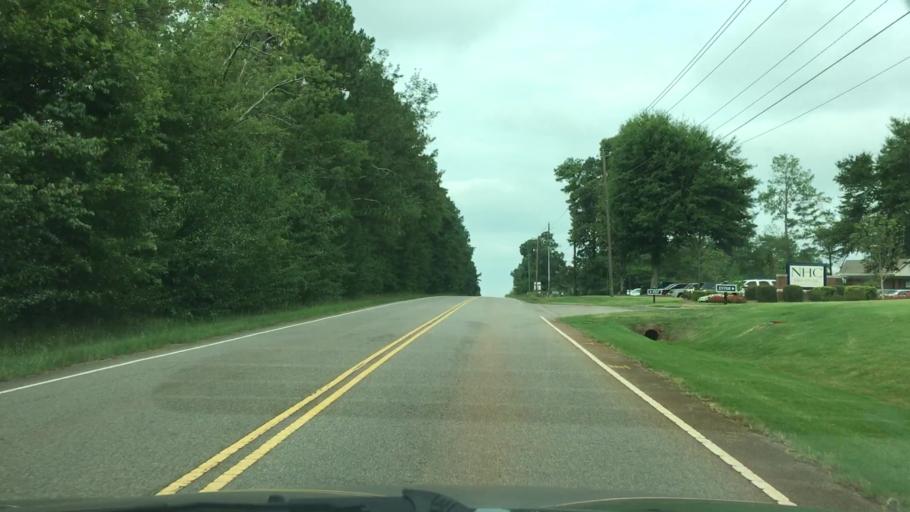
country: US
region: South Carolina
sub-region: Aiken County
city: Belvedere
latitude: 33.5610
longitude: -81.9427
